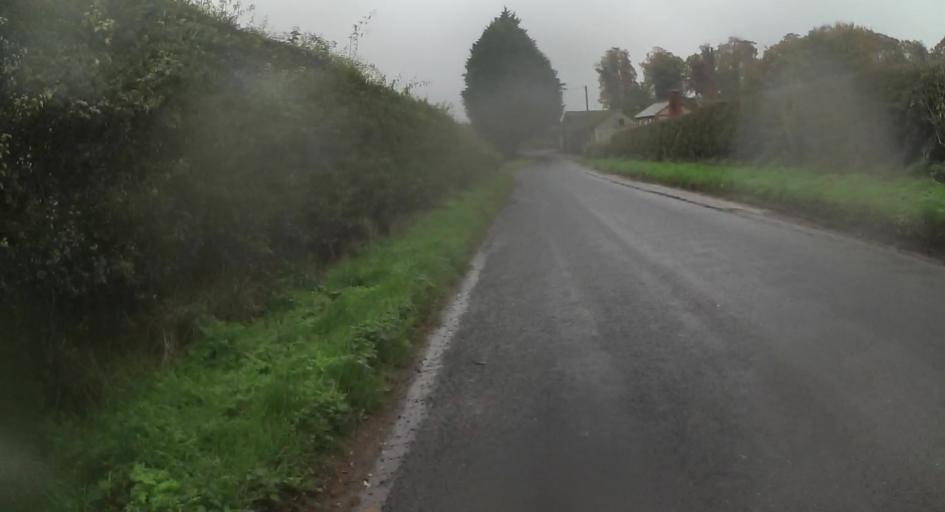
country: GB
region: England
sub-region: Hampshire
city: Four Marks
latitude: 51.1646
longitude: -1.1285
